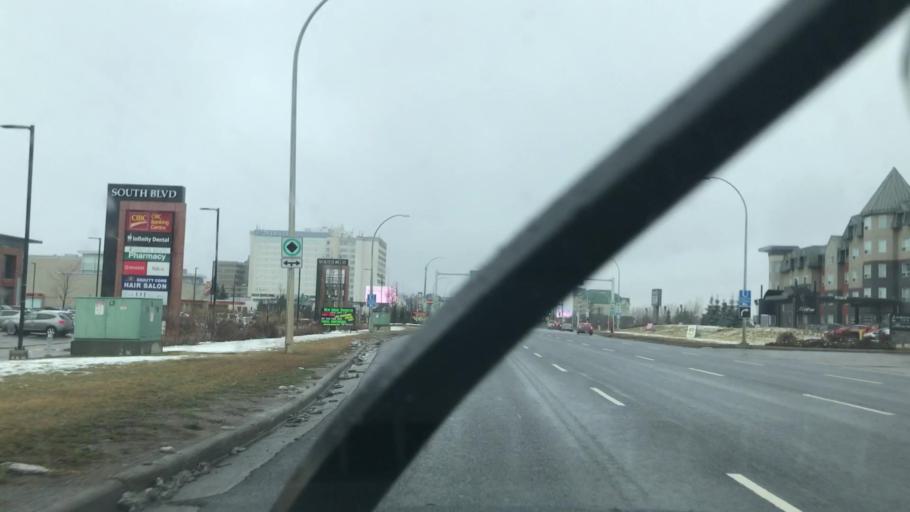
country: CA
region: Alberta
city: Edmonton
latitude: 53.4779
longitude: -113.4921
